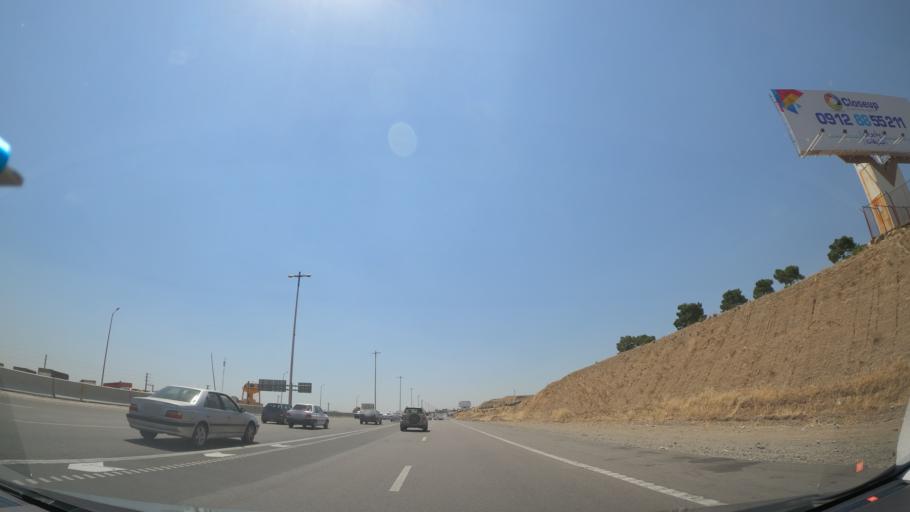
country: IR
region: Tehran
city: Shahr-e Qods
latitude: 35.7426
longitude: 51.1117
